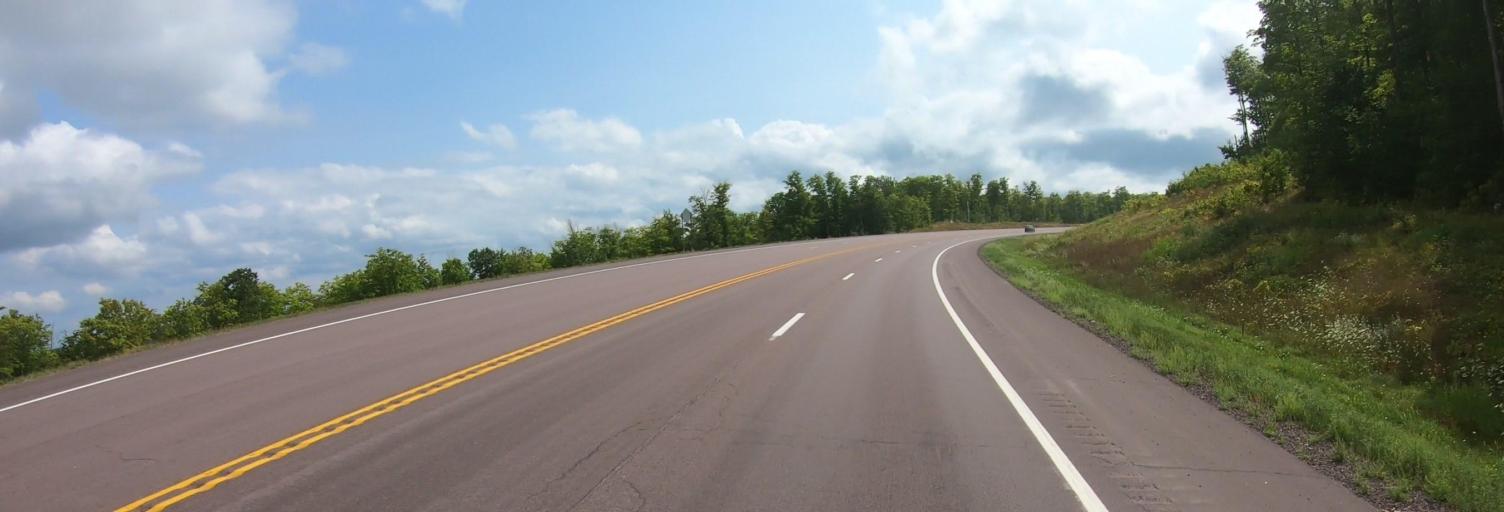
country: US
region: Michigan
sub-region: Houghton County
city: Hancock
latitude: 47.0640
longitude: -88.6404
